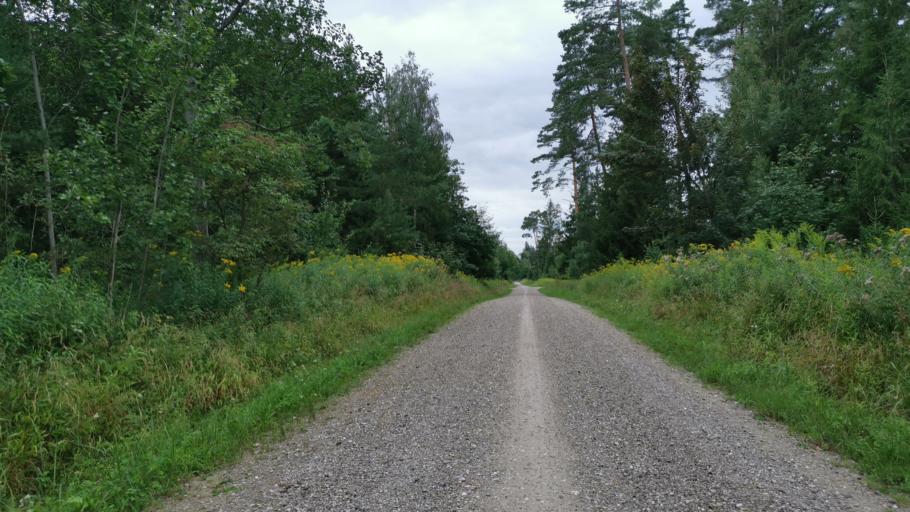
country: DE
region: Bavaria
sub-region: Upper Bavaria
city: Pullach im Isartal
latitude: 48.0695
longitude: 11.5655
